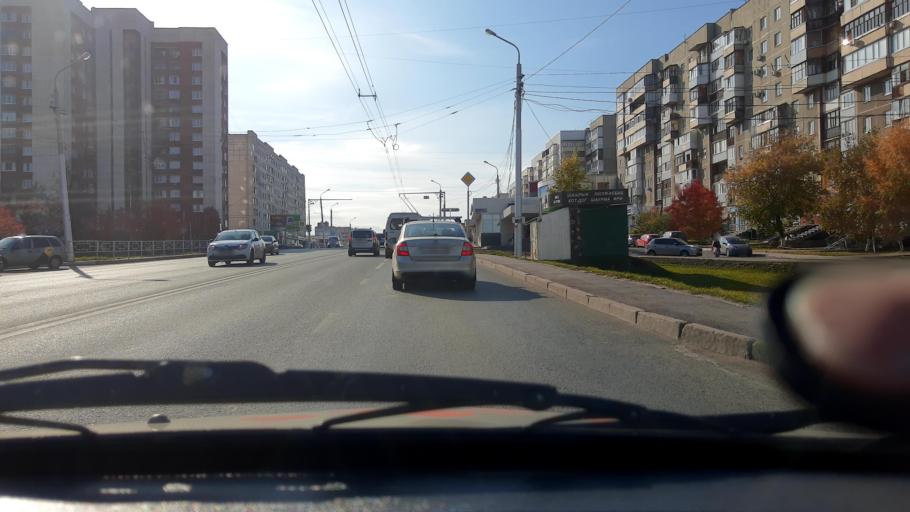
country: RU
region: Bashkortostan
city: Ufa
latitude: 54.7100
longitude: 56.0002
